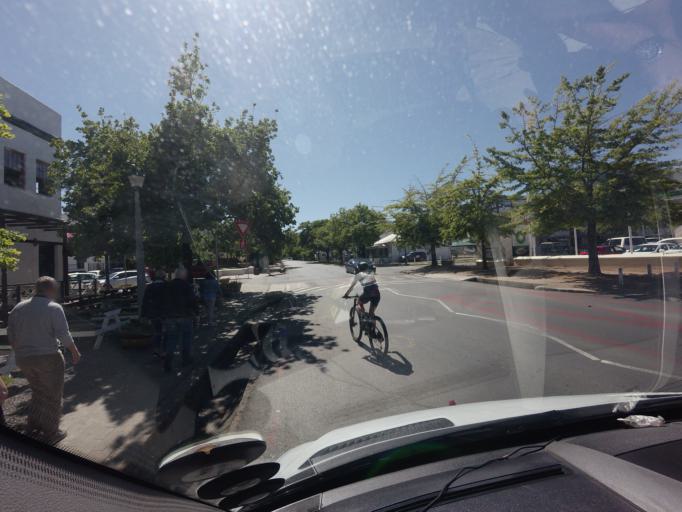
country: ZA
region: Western Cape
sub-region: Cape Winelands District Municipality
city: Stellenbosch
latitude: -33.9397
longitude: 18.8560
